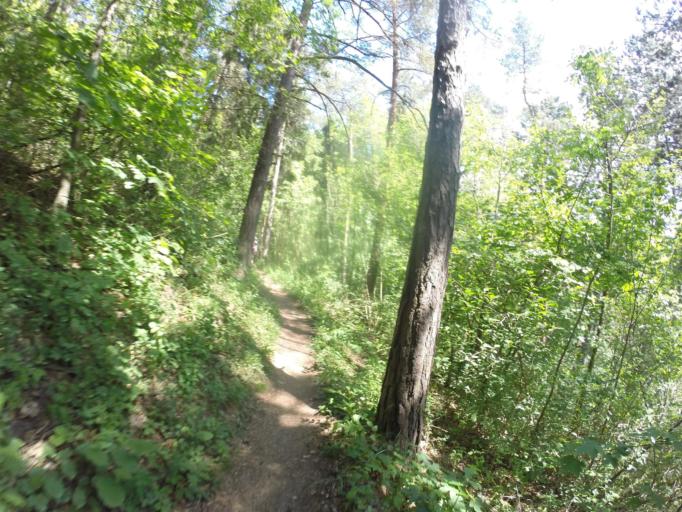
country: DE
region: Thuringia
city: Zollnitz
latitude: 50.8974
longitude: 11.6335
